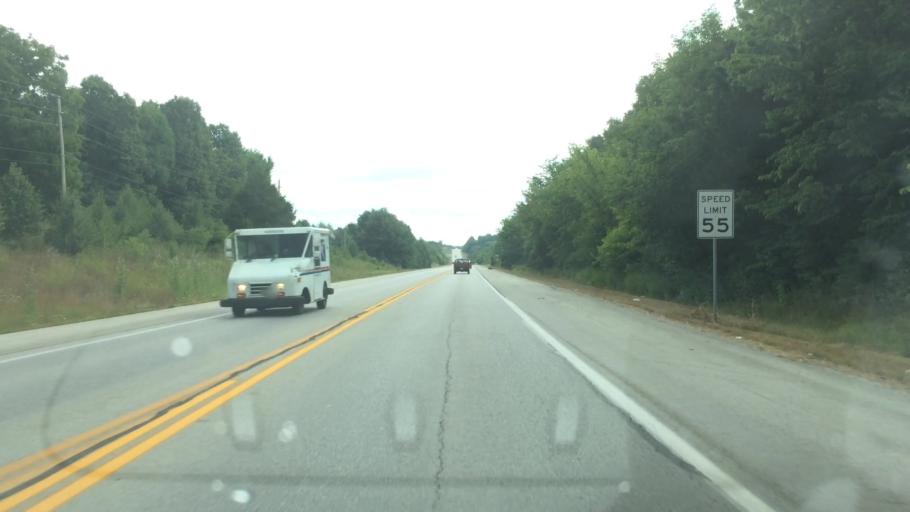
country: US
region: Missouri
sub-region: Greene County
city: Springfield
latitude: 37.1797
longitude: -93.2064
